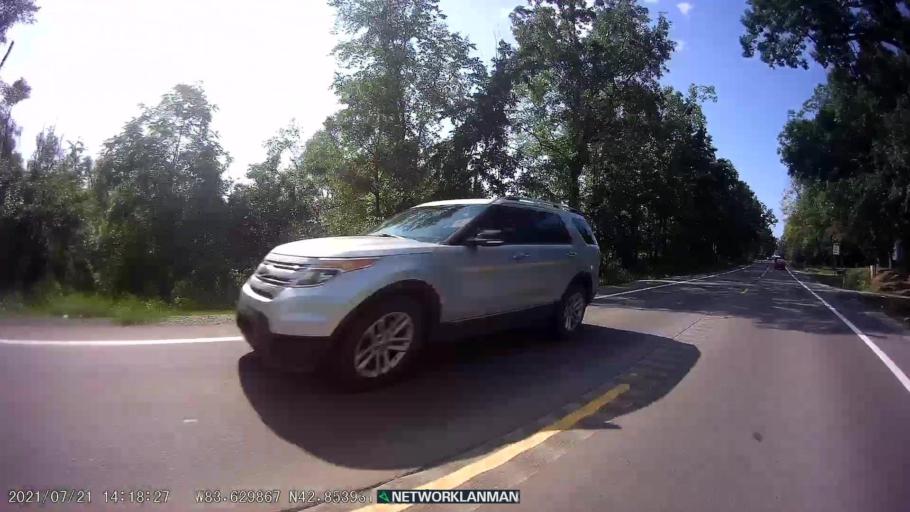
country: US
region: Michigan
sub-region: Oakland County
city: Holly
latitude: 42.8544
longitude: -83.6299
